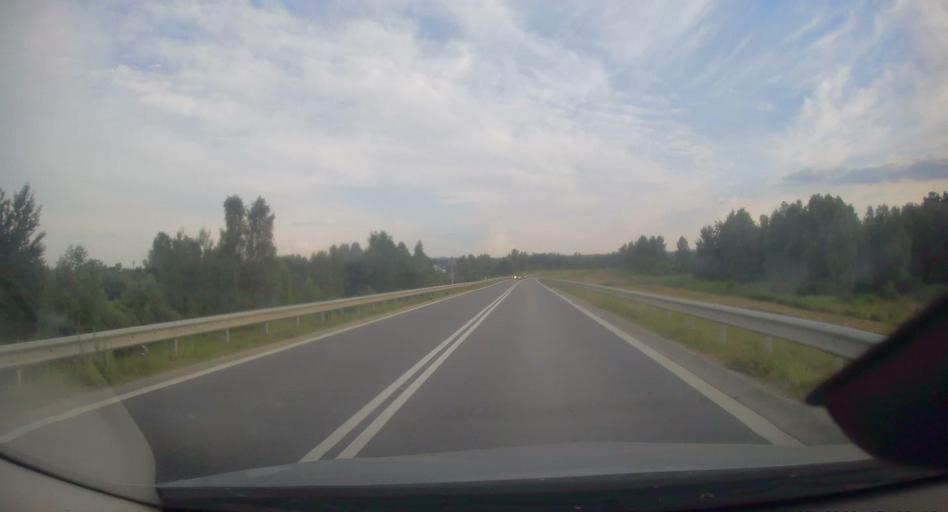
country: PL
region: Lesser Poland Voivodeship
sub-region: Powiat brzeski
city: Brzesko
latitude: 50.0021
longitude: 20.6009
